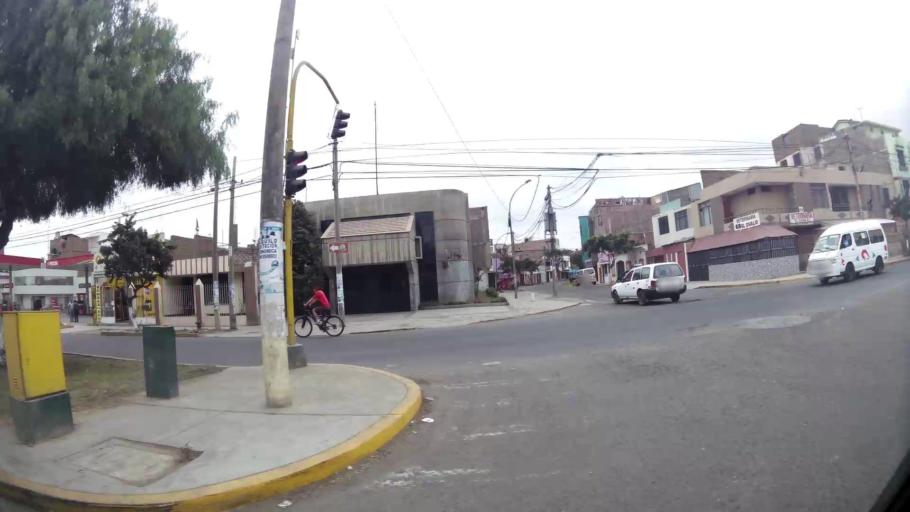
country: PE
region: La Libertad
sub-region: Provincia de Trujillo
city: Trujillo
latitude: -8.1209
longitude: -79.0203
